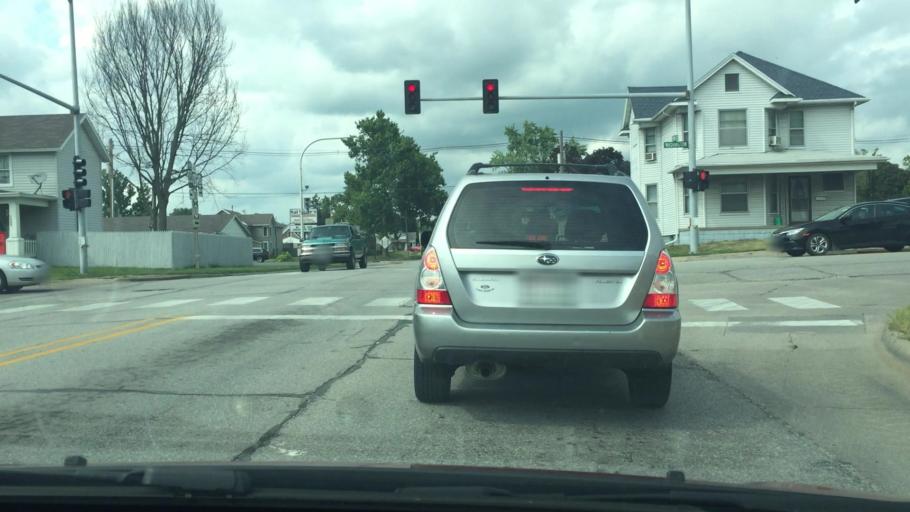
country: US
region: Iowa
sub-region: Muscatine County
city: Muscatine
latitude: 41.4351
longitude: -91.0308
